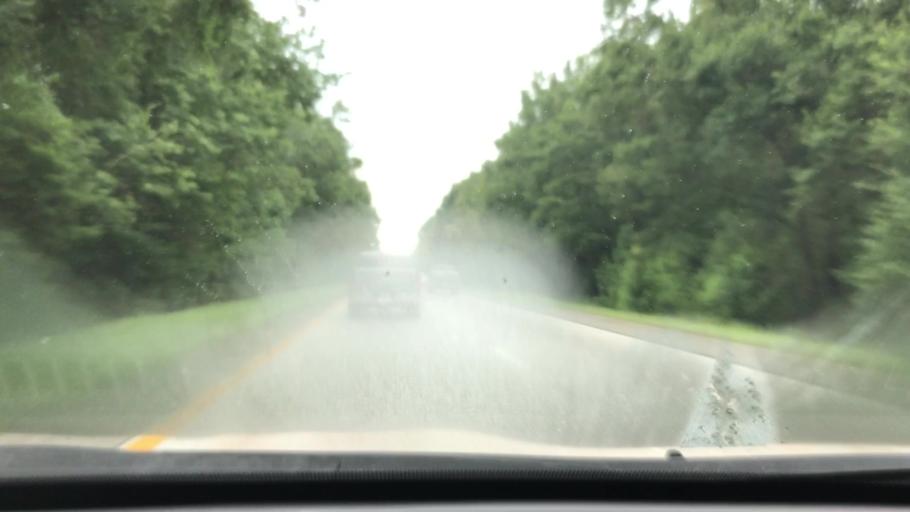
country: US
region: South Carolina
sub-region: Jasper County
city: Ridgeland
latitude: 32.3910
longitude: -81.0239
